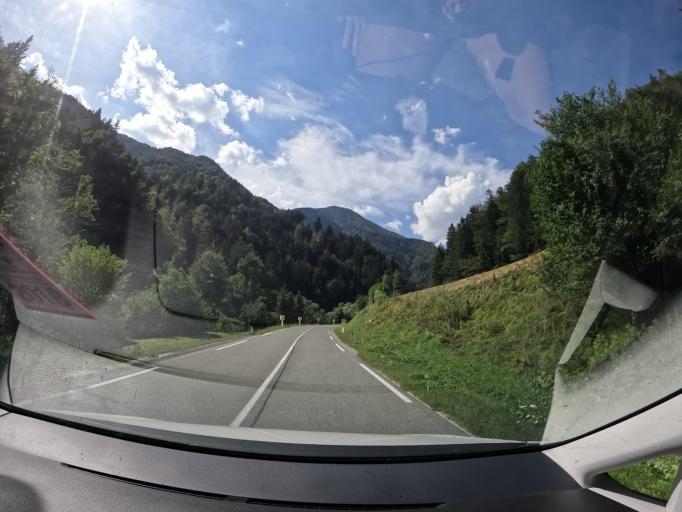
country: SI
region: Preddvor
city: Preddvor
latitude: 46.3626
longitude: 14.4383
